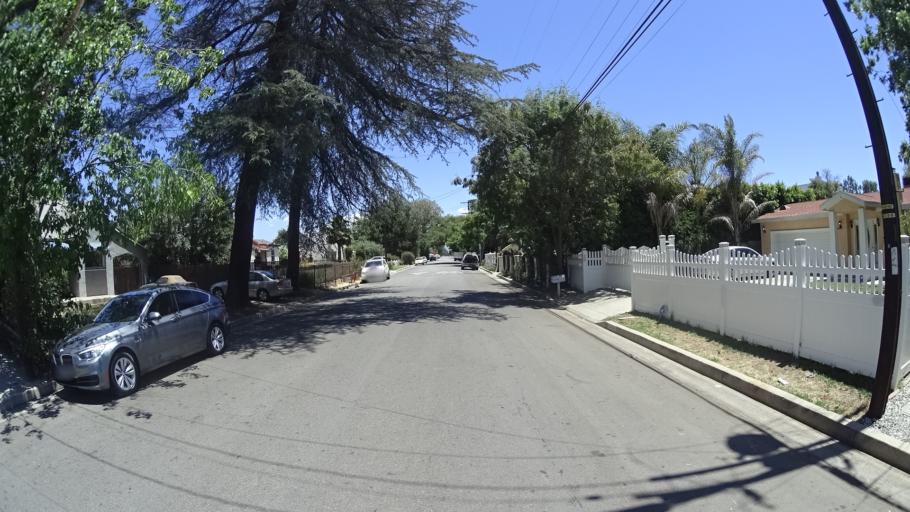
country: US
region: California
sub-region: Los Angeles County
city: Van Nuys
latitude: 34.2030
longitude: -118.4702
